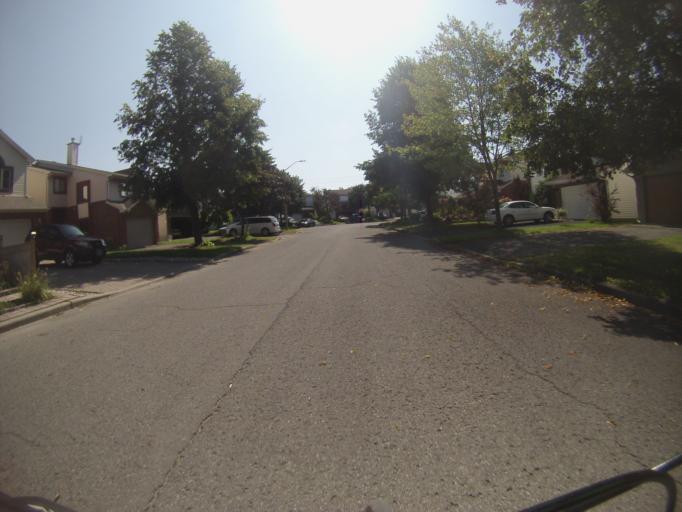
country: CA
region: Ontario
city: Ottawa
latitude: 45.3630
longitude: -75.6270
